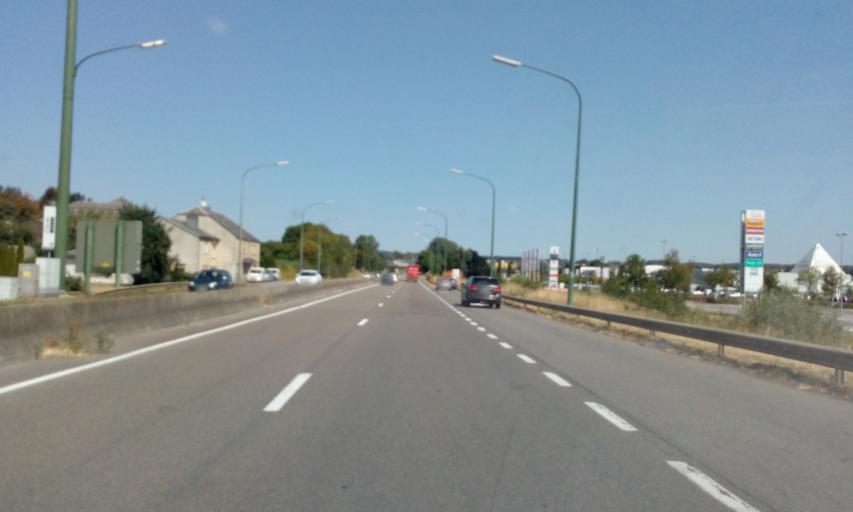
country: BE
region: Wallonia
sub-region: Province du Luxembourg
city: Messancy
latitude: 49.6099
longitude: 5.8108
